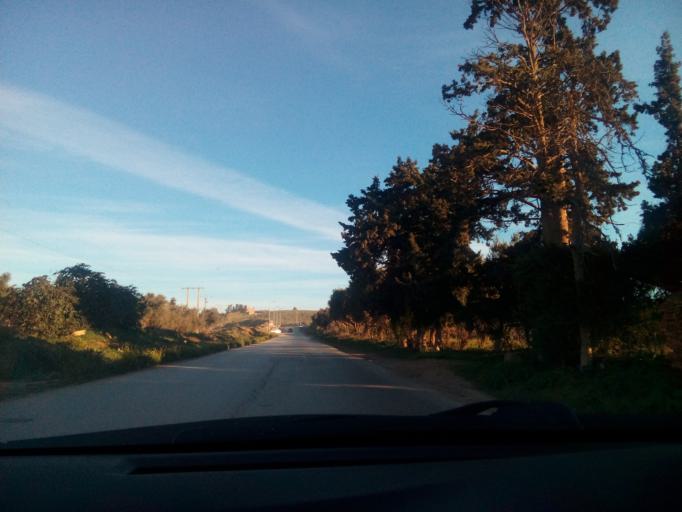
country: DZ
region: Oran
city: Es Senia
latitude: 35.6244
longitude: -0.6784
